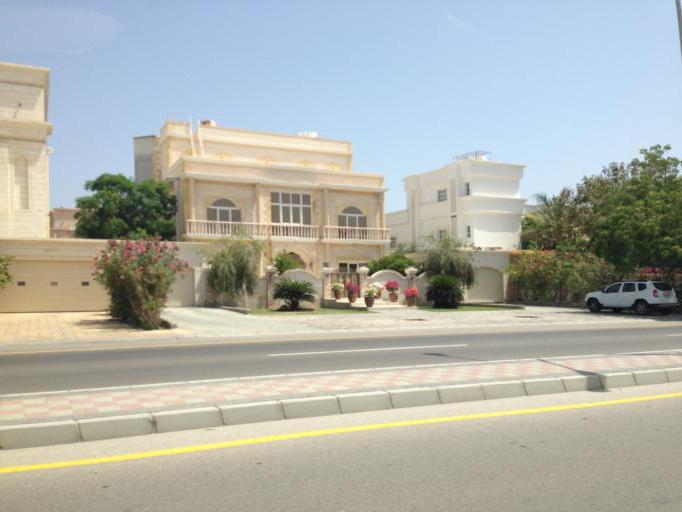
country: OM
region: Muhafazat Masqat
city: Bawshar
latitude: 23.6023
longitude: 58.3542
